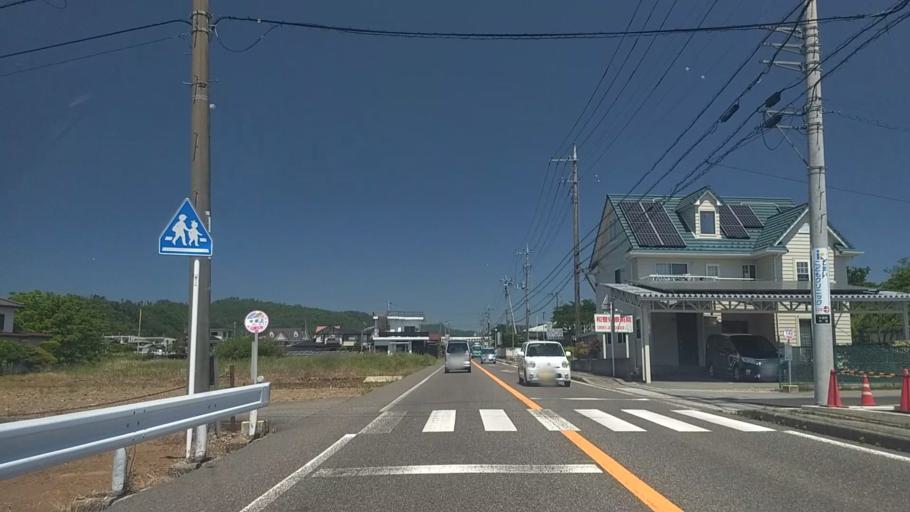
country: JP
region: Yamanashi
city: Nirasaki
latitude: 35.7452
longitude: 138.4407
